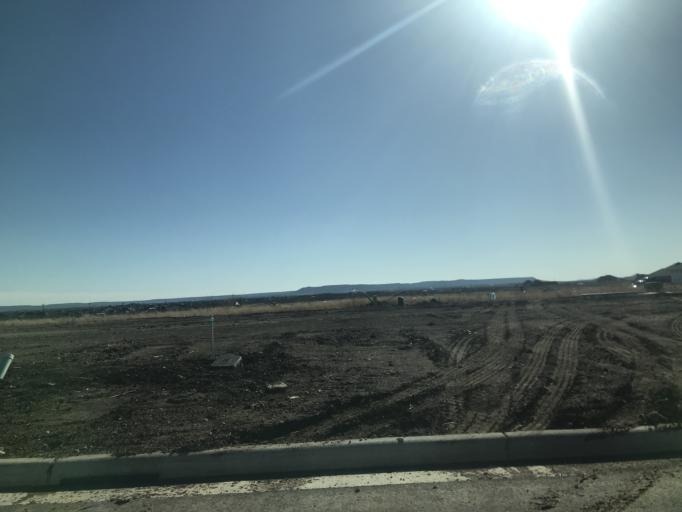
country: US
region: Texas
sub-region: Taylor County
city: Potosi
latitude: 32.3717
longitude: -99.7182
